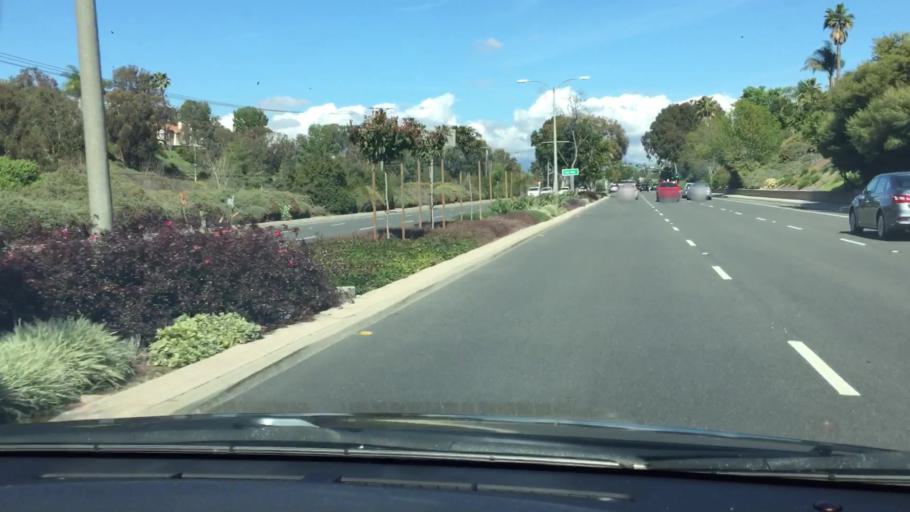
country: US
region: California
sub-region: Orange County
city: Laguna Niguel
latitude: 33.5347
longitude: -117.7003
